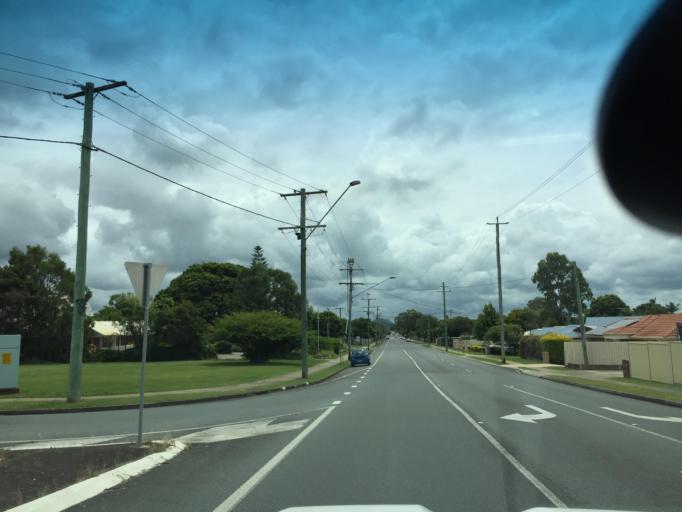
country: AU
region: Queensland
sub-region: Moreton Bay
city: Caboolture
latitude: -27.0782
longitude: 152.9317
